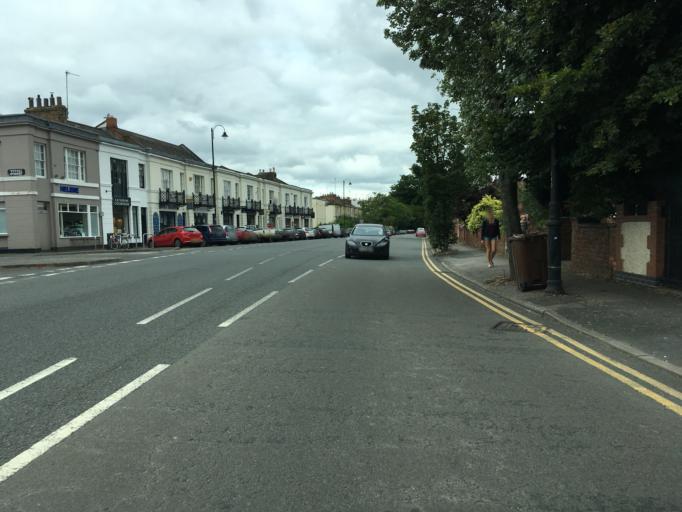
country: GB
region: England
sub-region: Gloucestershire
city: Cheltenham
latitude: 51.8924
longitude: -2.0862
